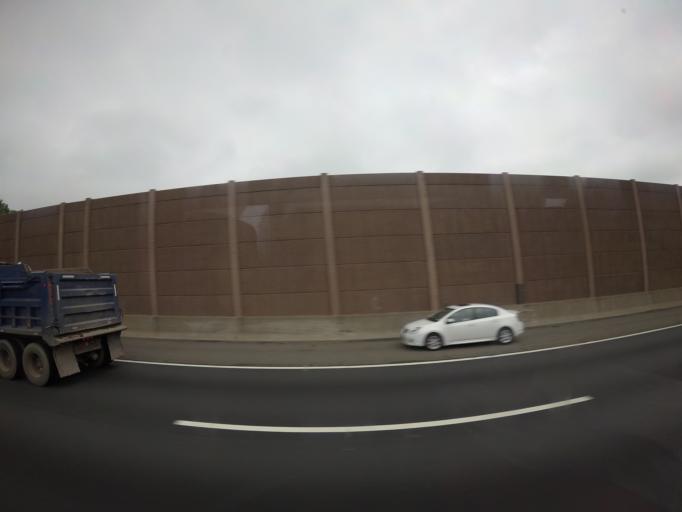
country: US
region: New Jersey
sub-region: Middlesex County
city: Carteret
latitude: 40.5831
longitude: -74.2415
